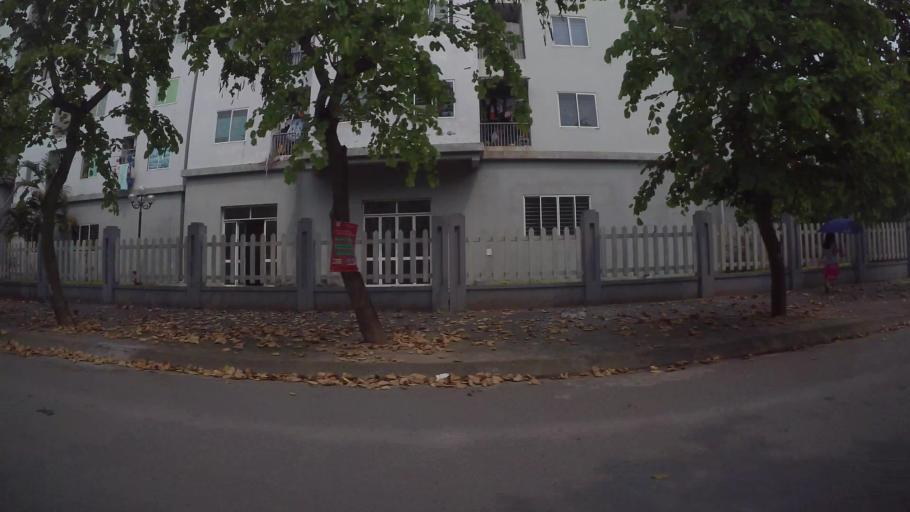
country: VN
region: Ha Noi
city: Trau Quy
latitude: 21.0566
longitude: 105.9103
